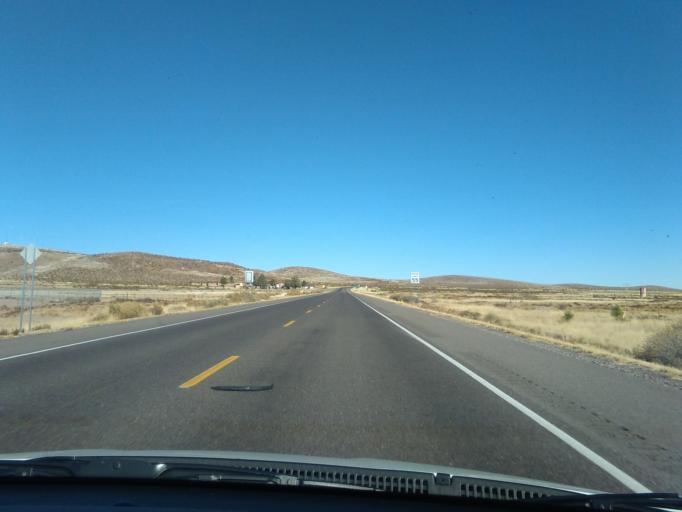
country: US
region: New Mexico
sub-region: Dona Ana County
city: Hatch
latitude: 32.5724
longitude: -107.4552
